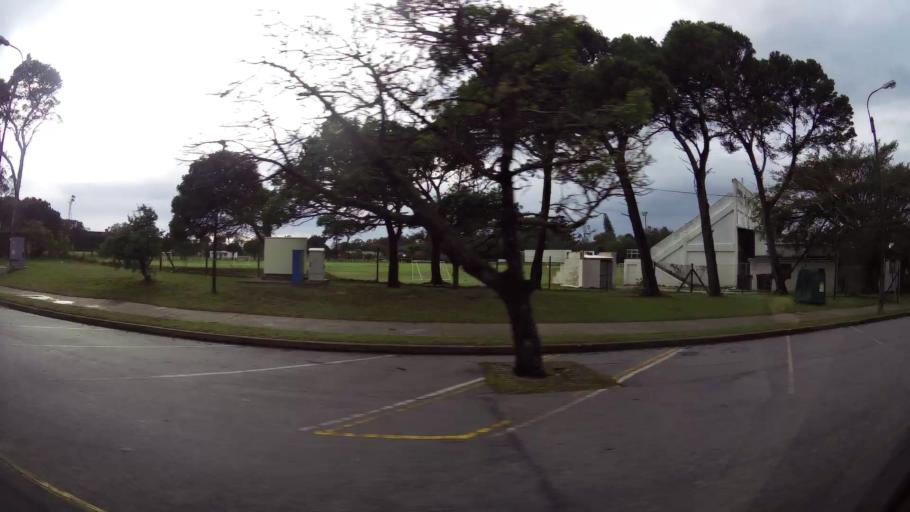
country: ZA
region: Eastern Cape
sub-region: Nelson Mandela Bay Metropolitan Municipality
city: Port Elizabeth
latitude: -33.9656
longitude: 25.6034
